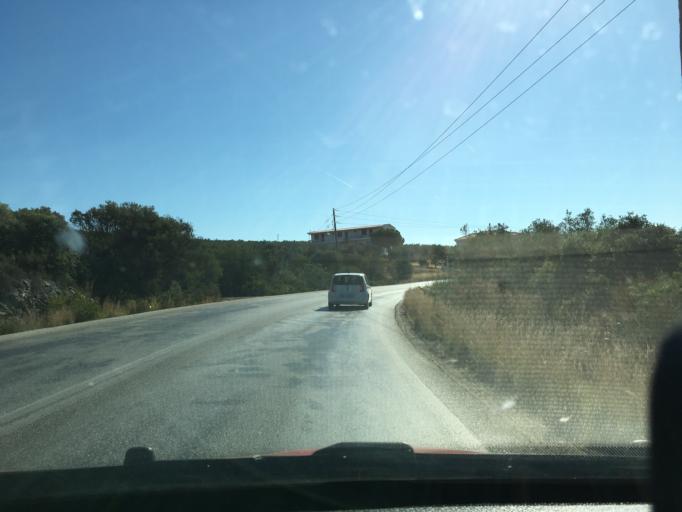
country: GR
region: Central Macedonia
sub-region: Nomos Chalkidikis
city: Kalyves Polygyrou
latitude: 40.2678
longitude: 23.4584
